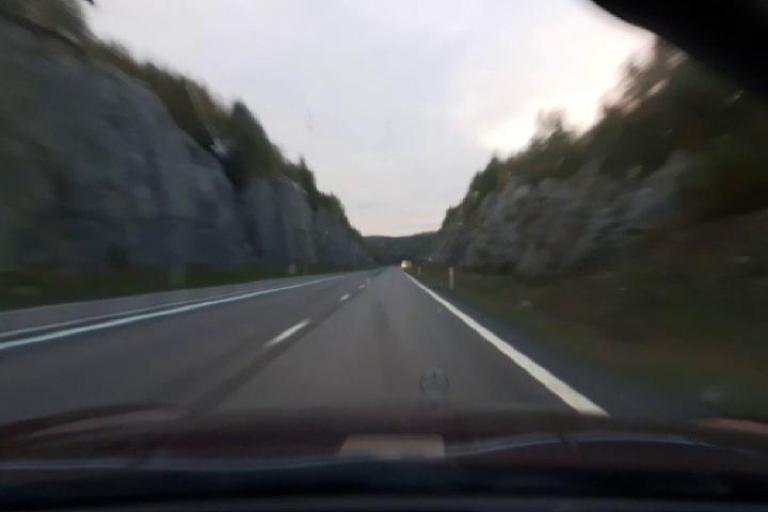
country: SE
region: Vaesternorrland
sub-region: Haernoesands Kommun
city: Haernoesand
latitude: 62.8342
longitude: 17.9679
